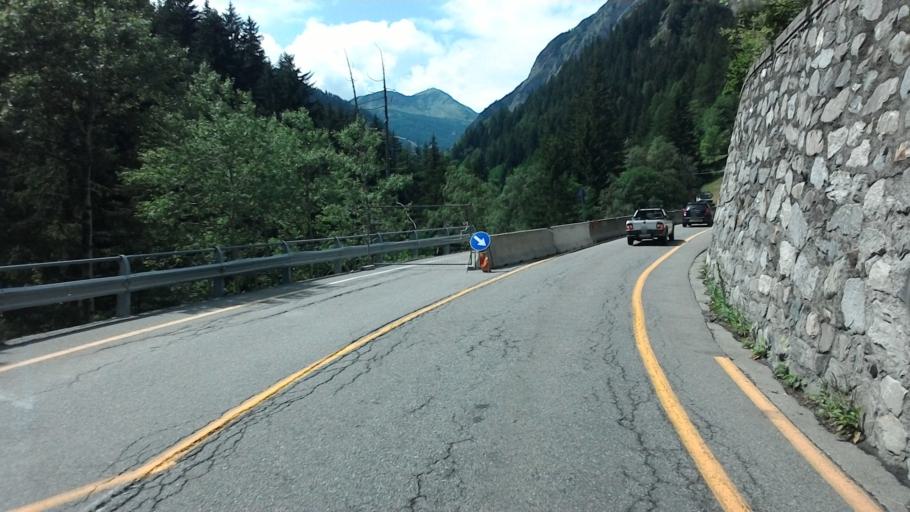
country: IT
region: Aosta Valley
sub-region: Valle d'Aosta
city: La Thuile
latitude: 45.7398
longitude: 6.9631
